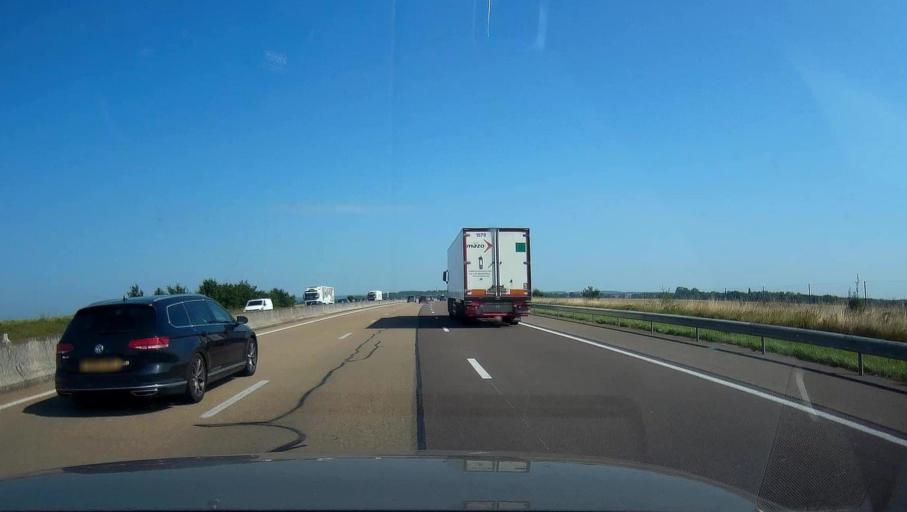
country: FR
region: Bourgogne
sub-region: Departement de la Cote-d'Or
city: Marcilly-sur-Tille
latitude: 47.4957
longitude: 5.1889
